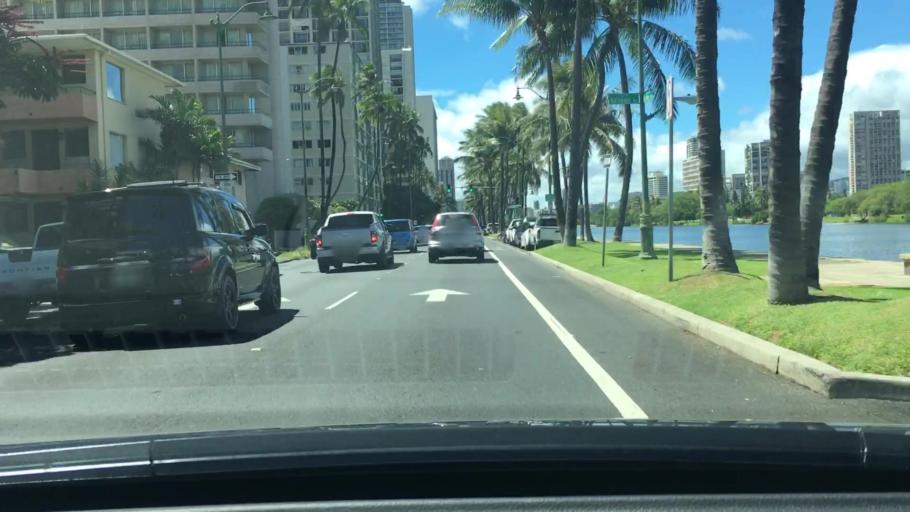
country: US
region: Hawaii
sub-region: Honolulu County
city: Honolulu
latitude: 21.2787
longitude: -157.8224
